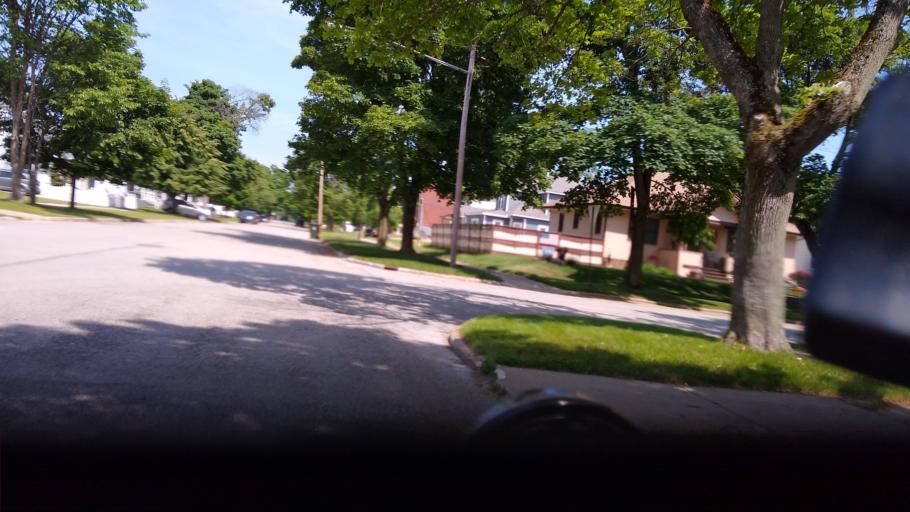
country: US
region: Michigan
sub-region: Delta County
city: Escanaba
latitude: 45.7372
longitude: -87.0644
